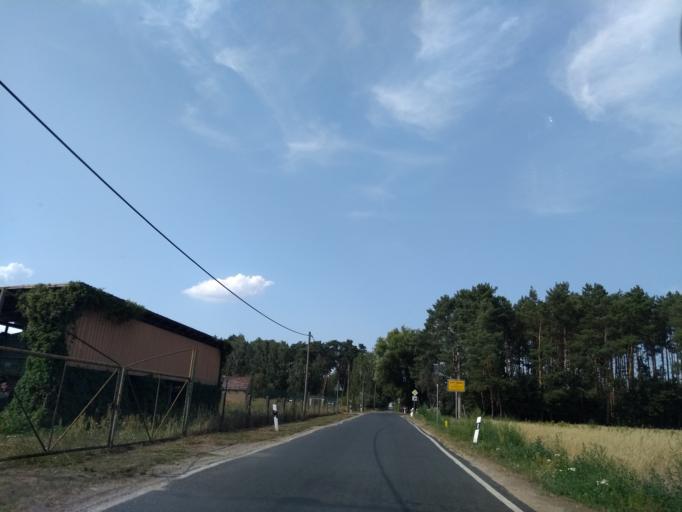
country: DE
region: Brandenburg
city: Luebben
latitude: 51.8651
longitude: 13.8523
